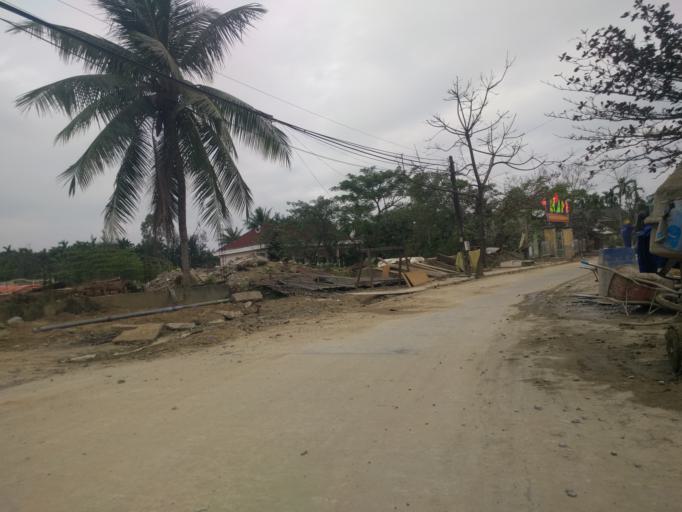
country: VN
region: Quang Nam
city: Hoi An
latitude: 15.8700
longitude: 108.3474
